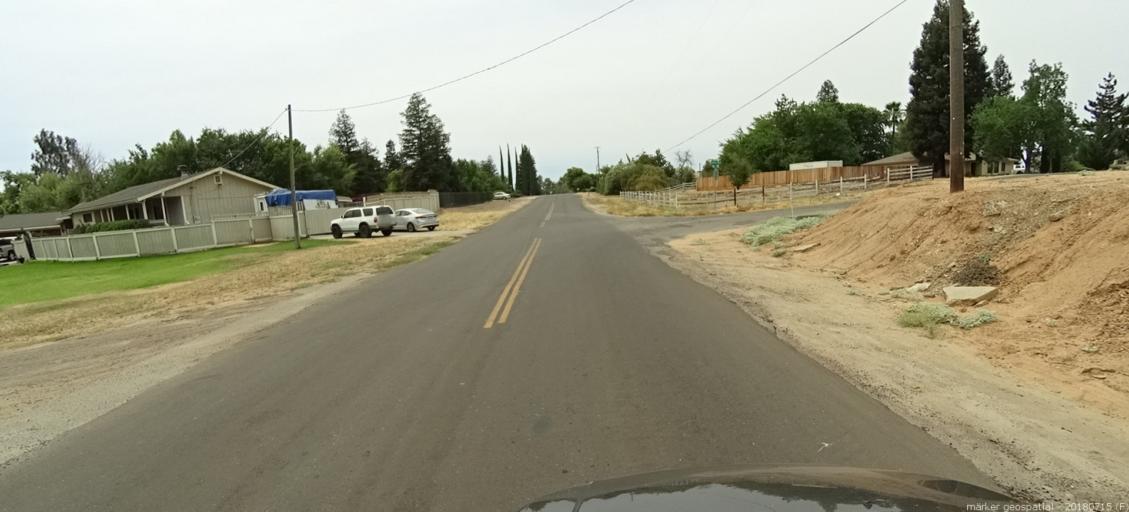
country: US
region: California
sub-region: Madera County
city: Madera Acres
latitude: 37.0109
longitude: -120.0827
